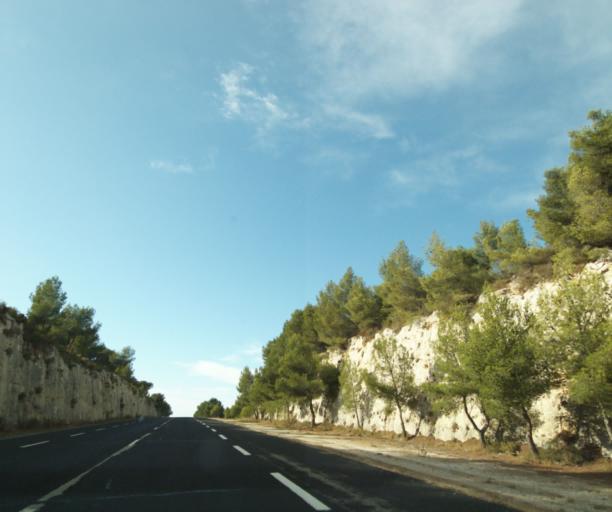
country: FR
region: Provence-Alpes-Cote d'Azur
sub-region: Departement des Bouches-du-Rhone
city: Sausset-les-Pins
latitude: 43.3453
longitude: 5.0767
